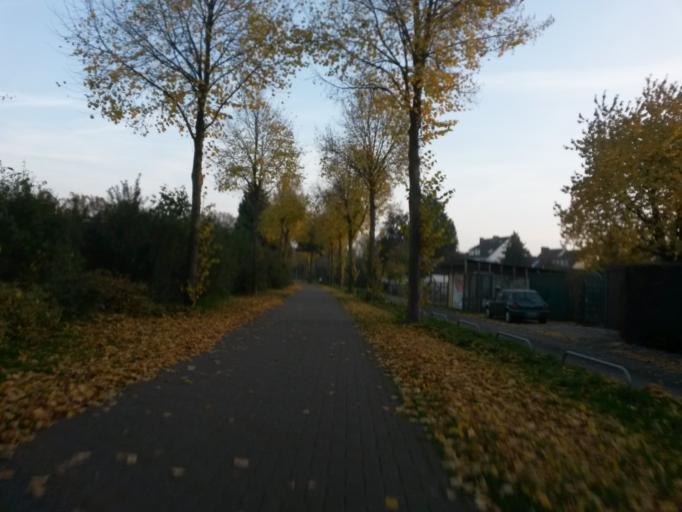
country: DE
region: Bremen
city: Bremen
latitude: 53.0580
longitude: 8.8145
